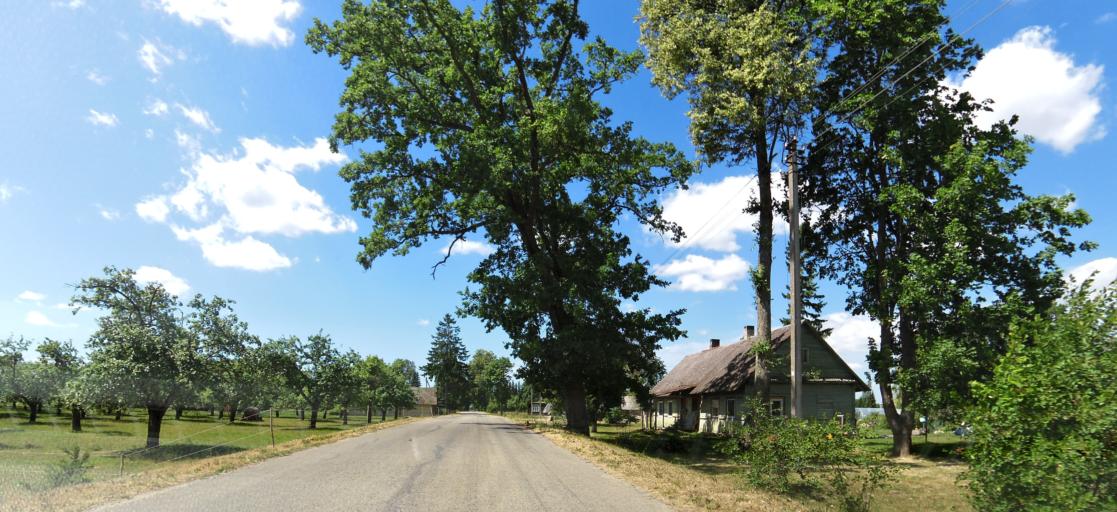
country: LT
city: Kupiskis
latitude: 55.9365
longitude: 24.9383
